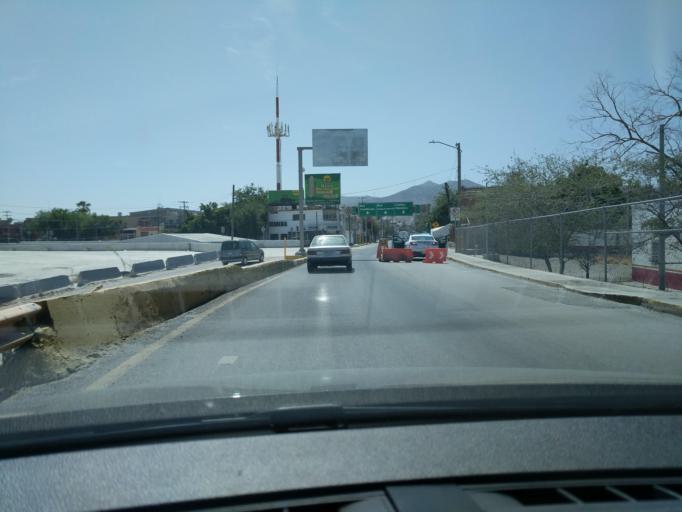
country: MX
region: Durango
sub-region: Lerdo
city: El Huarache (El Guarache)
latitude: 25.5448
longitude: -103.4689
